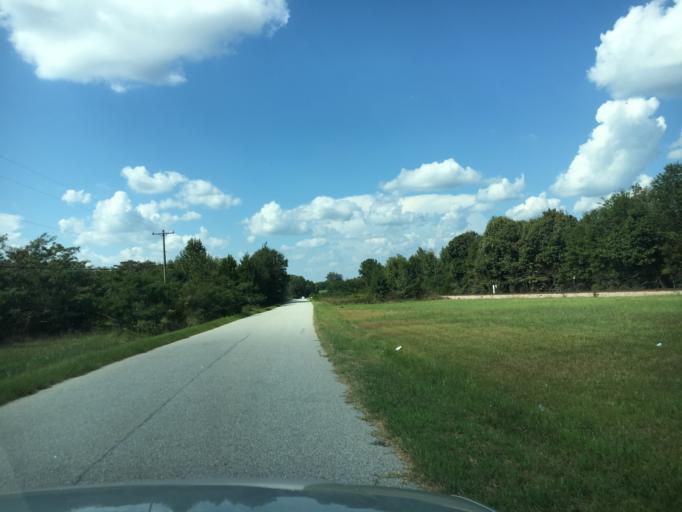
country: US
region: South Carolina
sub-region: Laurens County
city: Laurens
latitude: 34.5818
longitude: -82.1010
